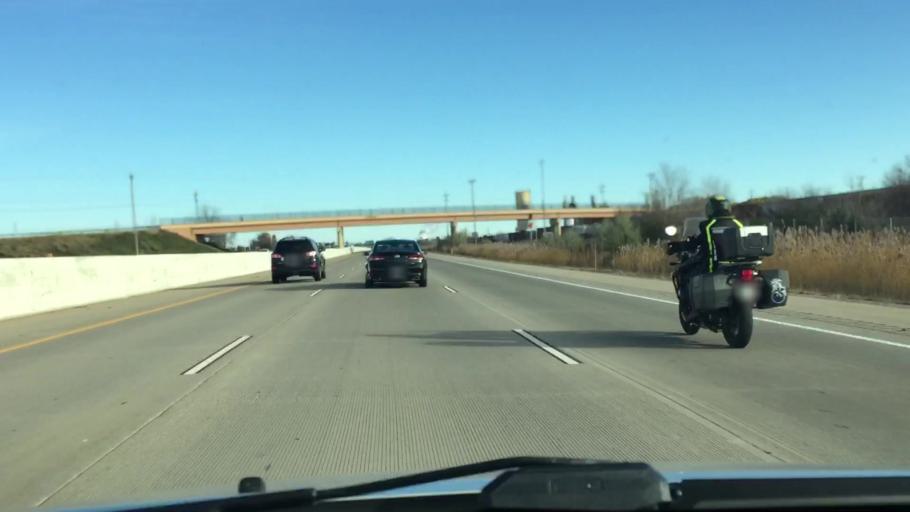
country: US
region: Wisconsin
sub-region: Winnebago County
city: Neenah
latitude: 44.1399
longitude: -88.4914
